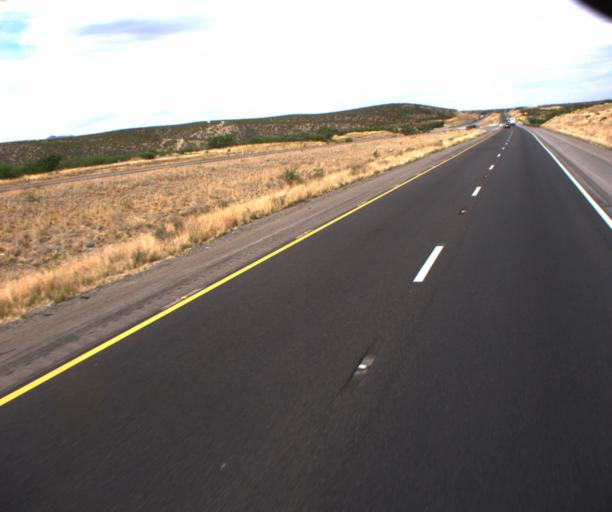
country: US
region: Arizona
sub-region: Cochise County
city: Mescal
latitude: 31.9855
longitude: -110.5630
